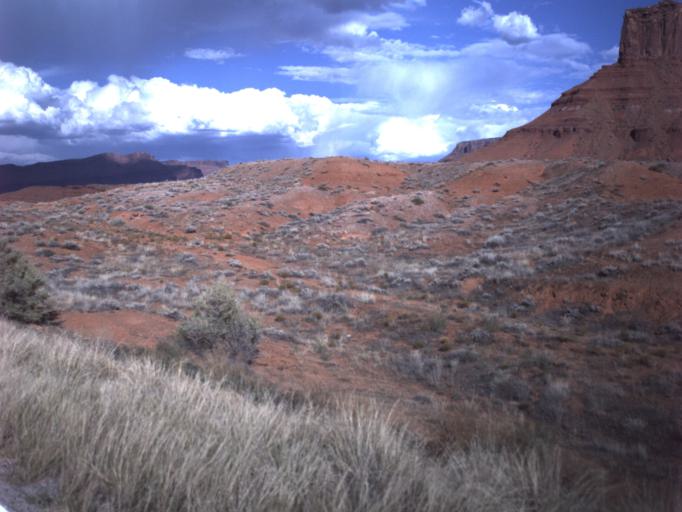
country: US
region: Utah
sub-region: Grand County
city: Moab
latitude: 38.6905
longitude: -109.4136
